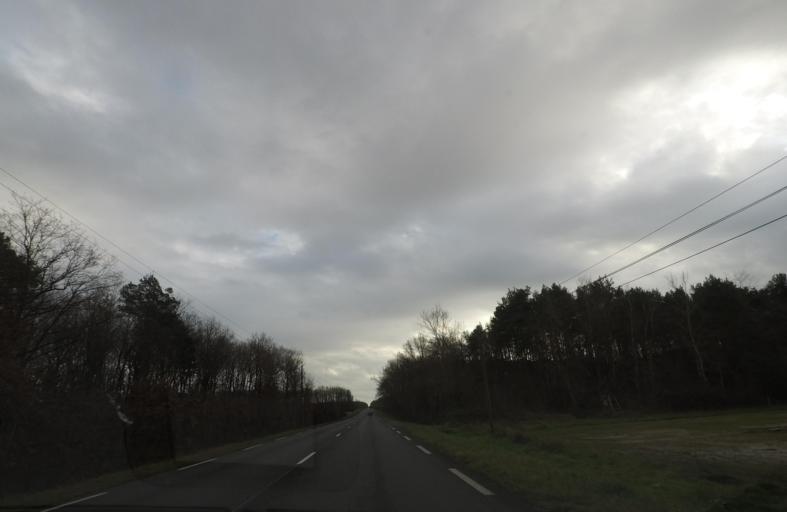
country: FR
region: Centre
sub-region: Departement du Loir-et-Cher
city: Mur-de-Sologne
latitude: 47.4278
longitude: 1.5722
